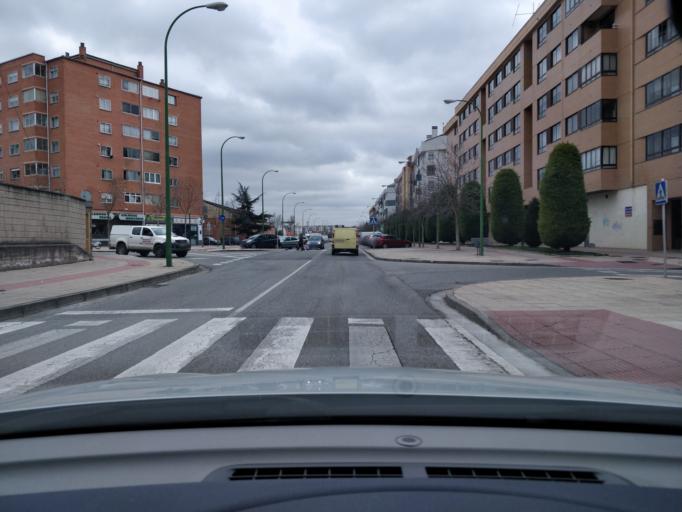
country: ES
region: Castille and Leon
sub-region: Provincia de Burgos
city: Burgos
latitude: 42.3641
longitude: -3.6558
